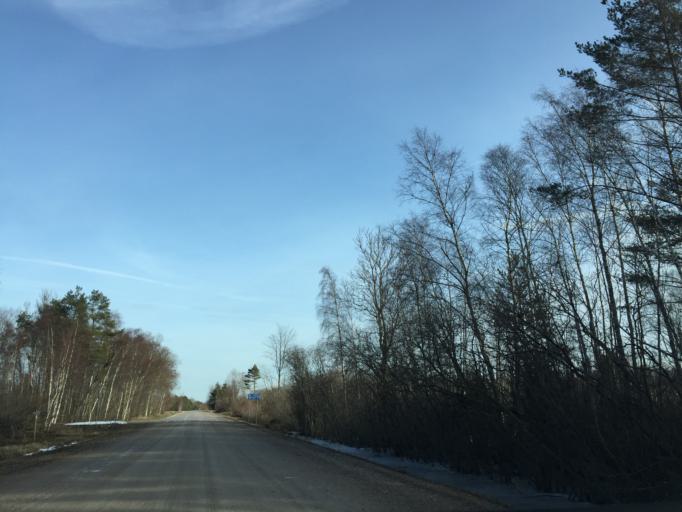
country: EE
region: Saare
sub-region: Kuressaare linn
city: Kuressaare
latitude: 58.3194
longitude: 21.9961
